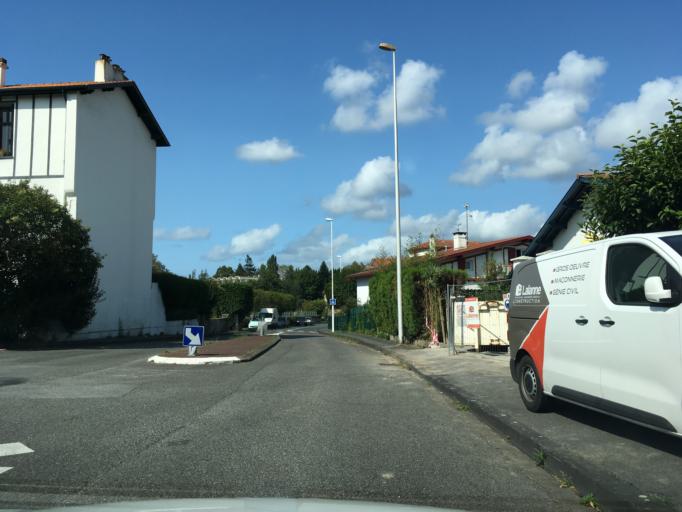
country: FR
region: Aquitaine
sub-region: Departement des Pyrenees-Atlantiques
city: Bayonne
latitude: 43.4821
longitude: -1.4876
